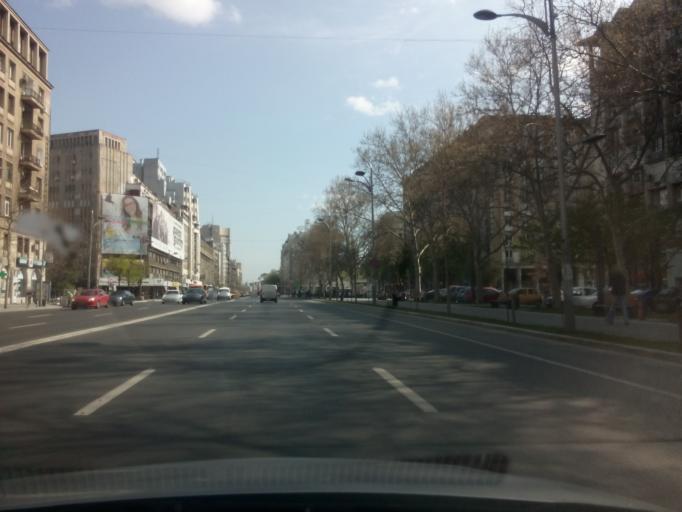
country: RO
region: Bucuresti
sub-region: Municipiul Bucuresti
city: Bucharest
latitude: 44.4437
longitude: 26.0983
